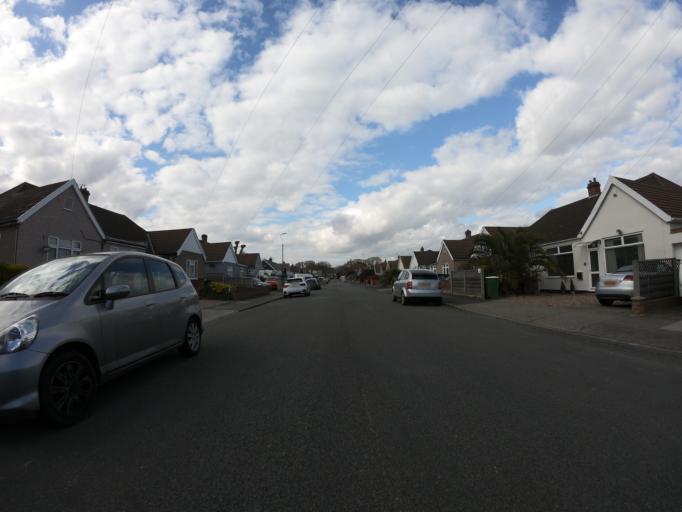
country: GB
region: England
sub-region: Greater London
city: Belvedere
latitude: 51.4818
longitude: 0.1404
